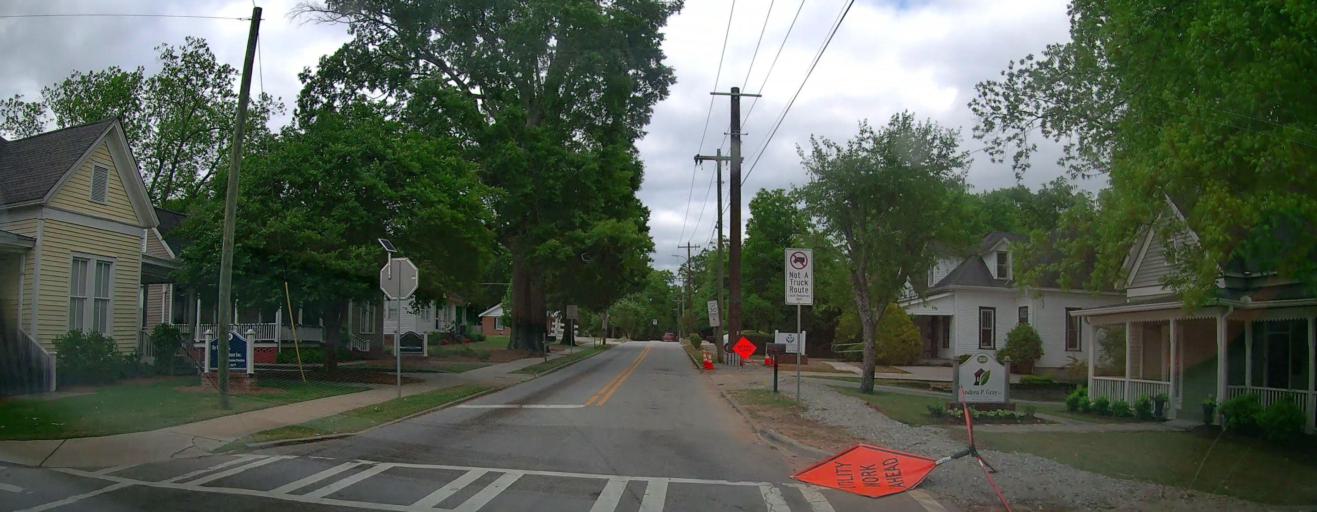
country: US
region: Georgia
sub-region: Walton County
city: Monroe
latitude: 33.7926
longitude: -83.7104
